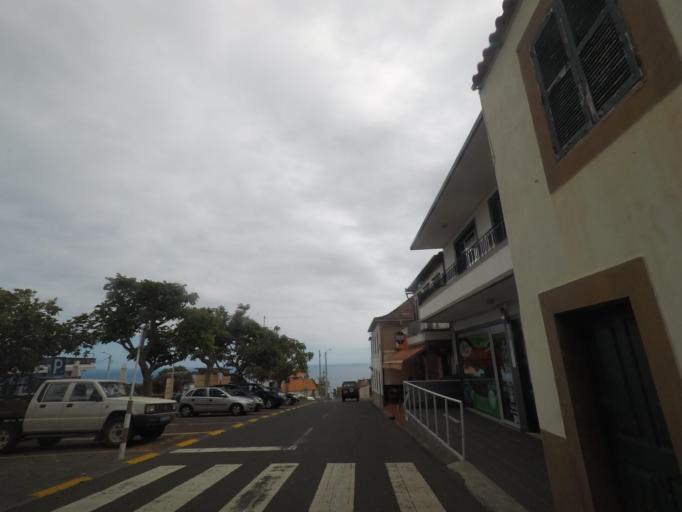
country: PT
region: Madeira
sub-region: Calheta
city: Arco da Calheta
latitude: 32.7136
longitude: -17.1477
